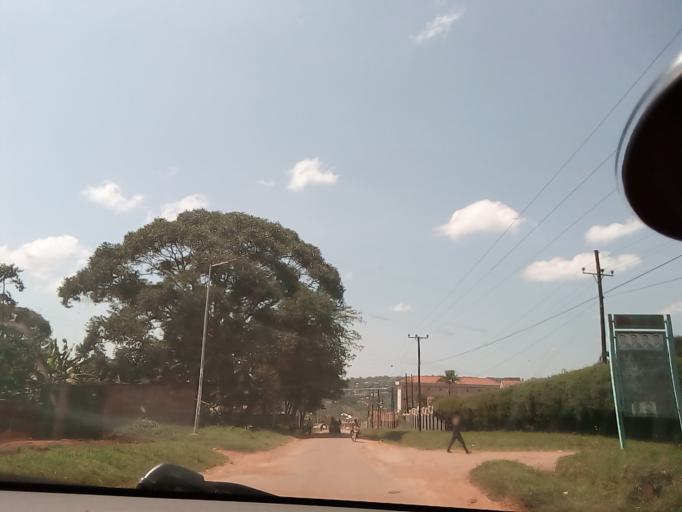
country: UG
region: Central Region
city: Masaka
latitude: -0.3312
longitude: 31.7396
